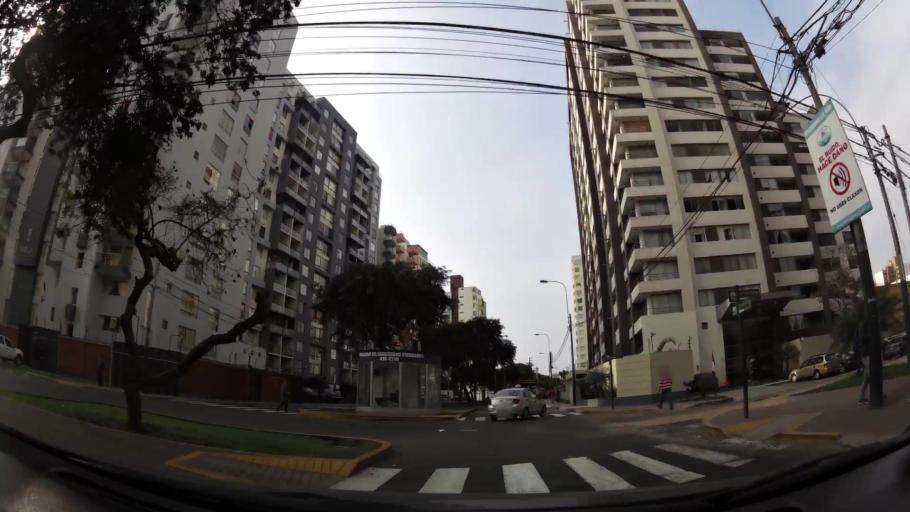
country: PE
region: Lima
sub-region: Lima
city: San Isidro
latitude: -12.0922
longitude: -77.0590
